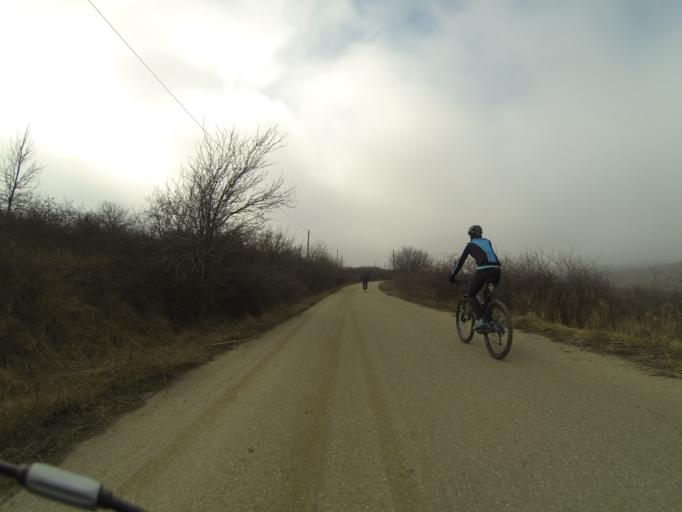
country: RO
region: Mehedinti
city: Dumbrava de Sus
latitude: 44.4930
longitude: 23.0879
